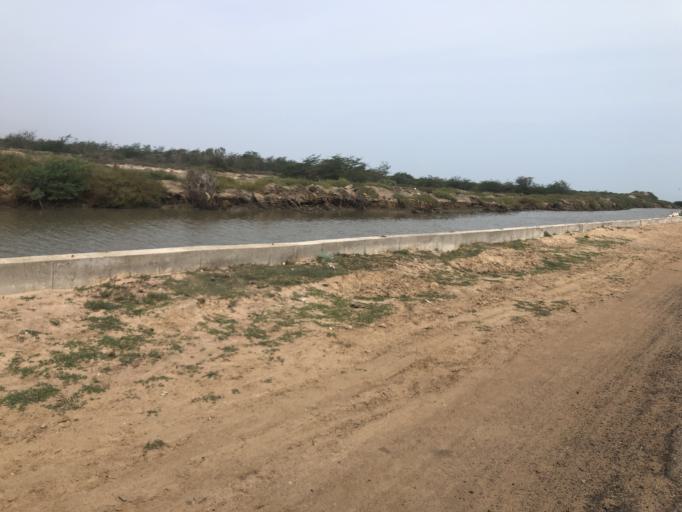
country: IN
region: Tamil Nadu
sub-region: Thanjavur
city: Adirampattinam
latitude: 10.3180
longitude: 79.3813
